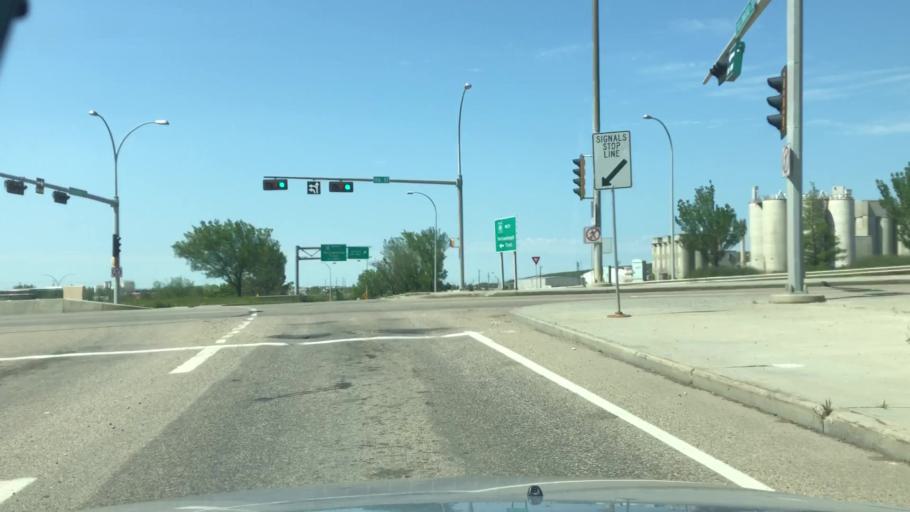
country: CA
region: Alberta
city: St. Albert
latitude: 53.5798
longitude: -113.5906
